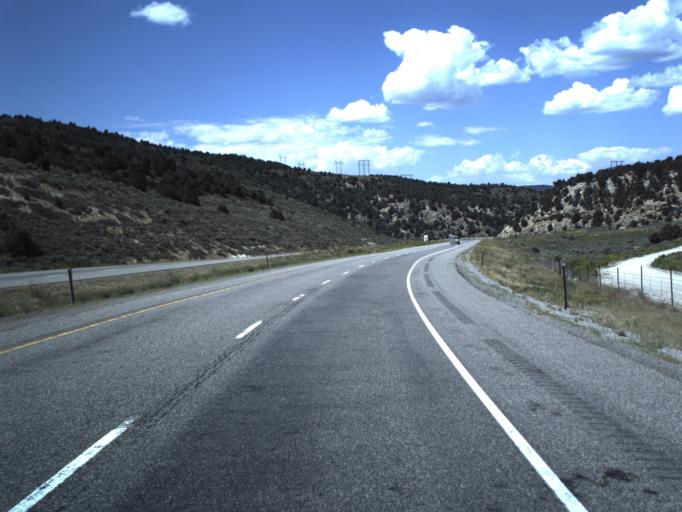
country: US
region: Utah
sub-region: Sevier County
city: Salina
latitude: 38.8054
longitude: -111.5284
